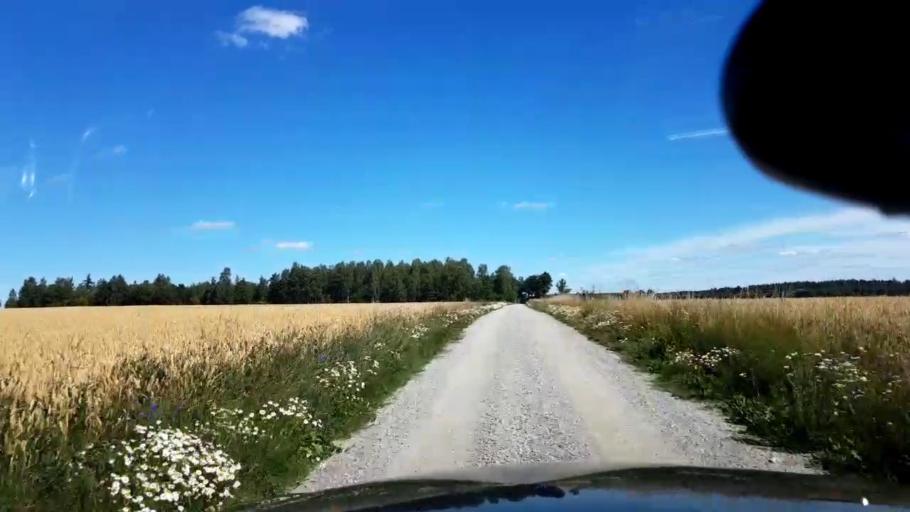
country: SE
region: Stockholm
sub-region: Upplands-Bro Kommun
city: Bro
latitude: 59.5920
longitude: 17.6390
